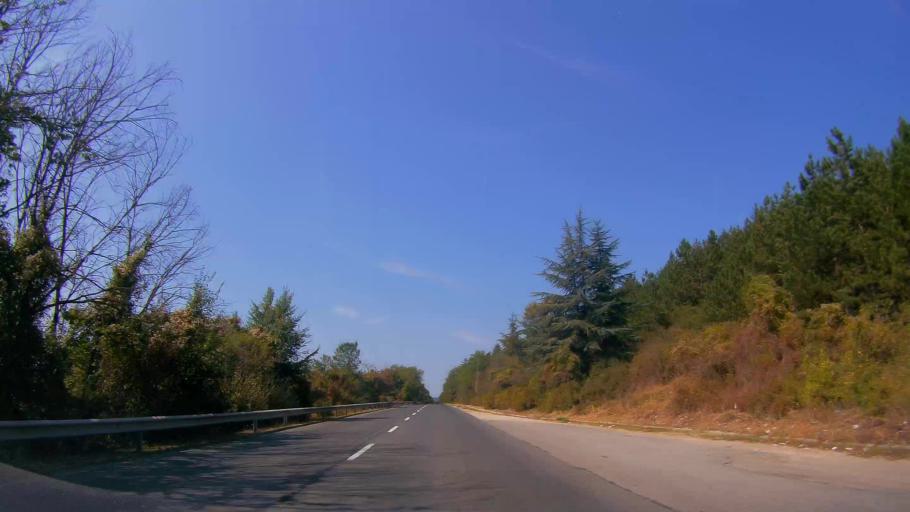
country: BG
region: Shumen
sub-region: Obshtina Shumen
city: Shumen
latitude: 43.3044
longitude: 26.9492
